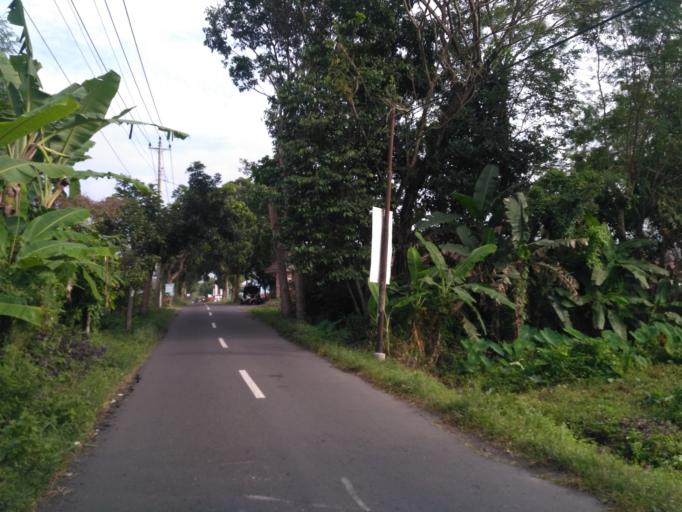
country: ID
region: Daerah Istimewa Yogyakarta
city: Melati
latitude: -7.7105
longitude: 110.3953
